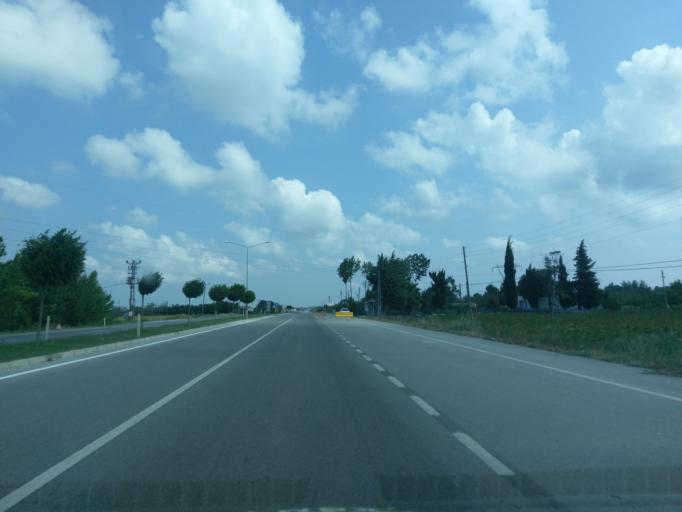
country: TR
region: Samsun
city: Bafra
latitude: 41.6006
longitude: 35.7899
